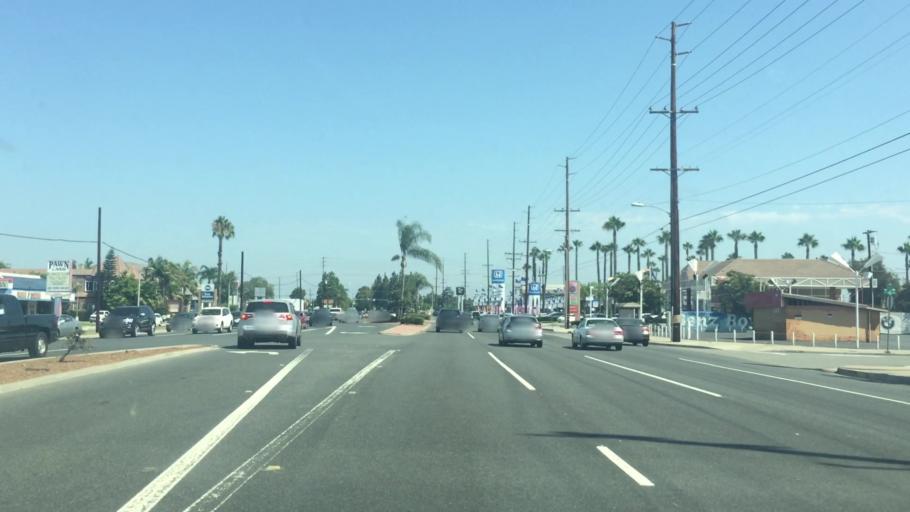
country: US
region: California
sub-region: Orange County
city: Westminster
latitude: 33.7626
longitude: -117.9896
